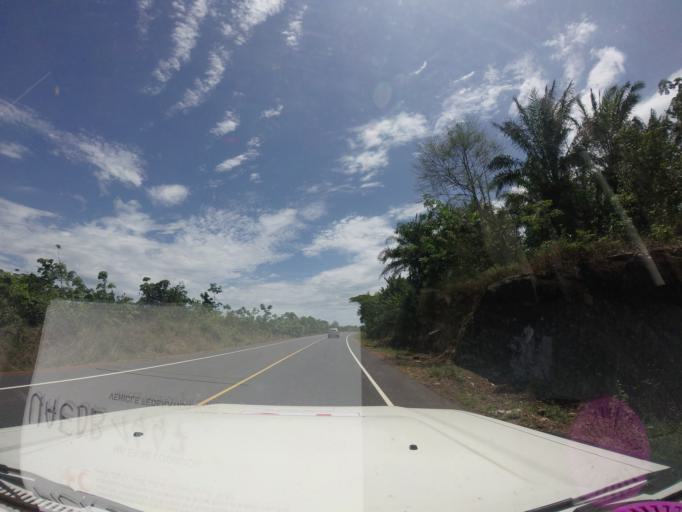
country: LR
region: Margibi
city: Kakata
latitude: 6.5181
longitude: -10.3866
